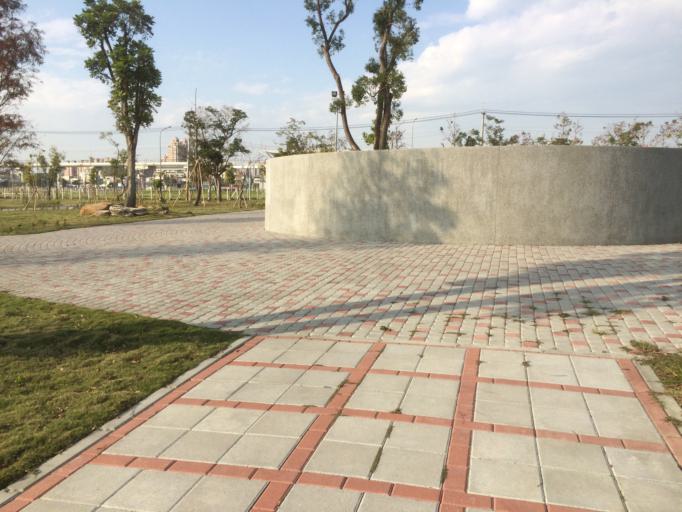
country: TW
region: Taiwan
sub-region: Taichung City
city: Taichung
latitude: 24.1794
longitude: 120.7081
